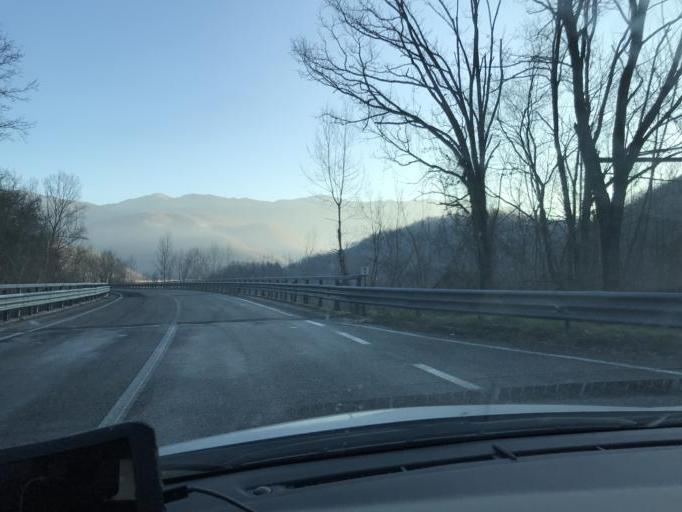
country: IT
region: Latium
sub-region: Provincia di Rieti
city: Concerviano
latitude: 42.3317
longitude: 12.9912
